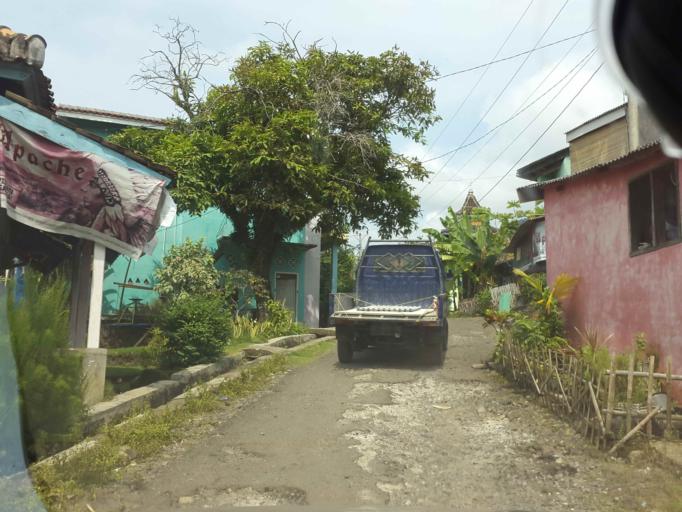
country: ID
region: Lampung
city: Penengahan
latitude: -5.8265
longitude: 105.6659
